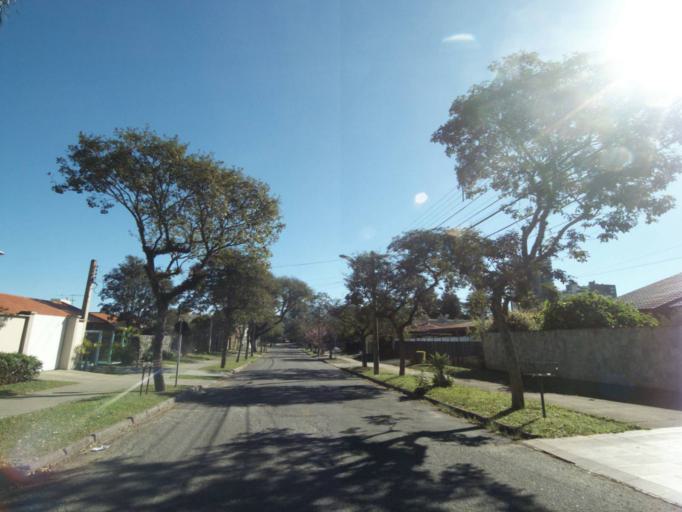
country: BR
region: Parana
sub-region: Curitiba
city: Curitiba
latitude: -25.4126
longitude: -49.2439
